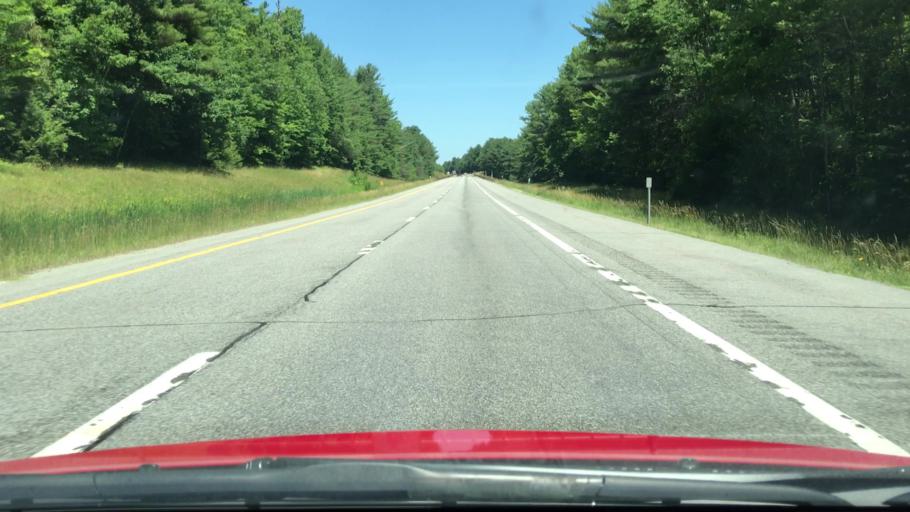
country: US
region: New York
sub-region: Essex County
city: Elizabethtown
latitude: 44.1451
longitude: -73.5836
